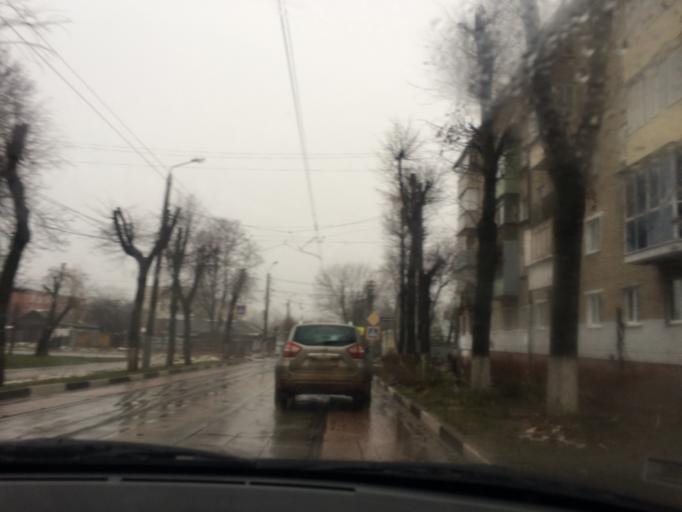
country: RU
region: Tula
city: Tula
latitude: 54.1842
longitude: 37.6038
